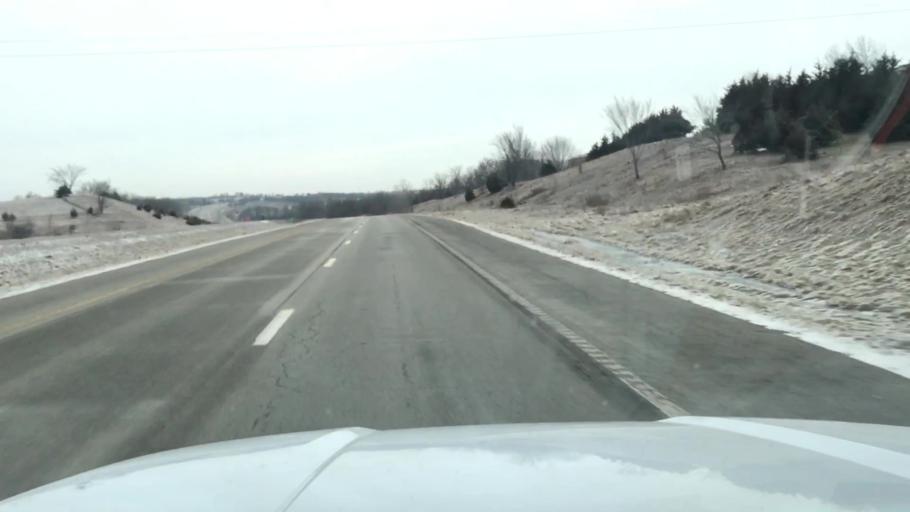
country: US
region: Missouri
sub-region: Andrew County
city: Savannah
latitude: 39.8993
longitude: -94.8570
